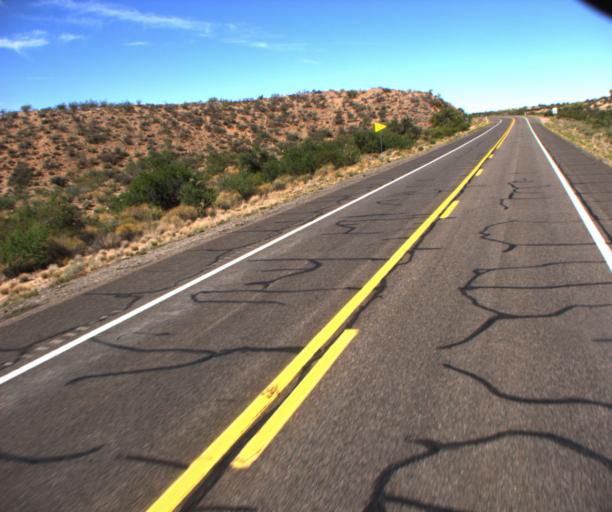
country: US
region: Arizona
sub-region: Yavapai County
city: Congress
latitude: 34.1659
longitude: -112.8388
